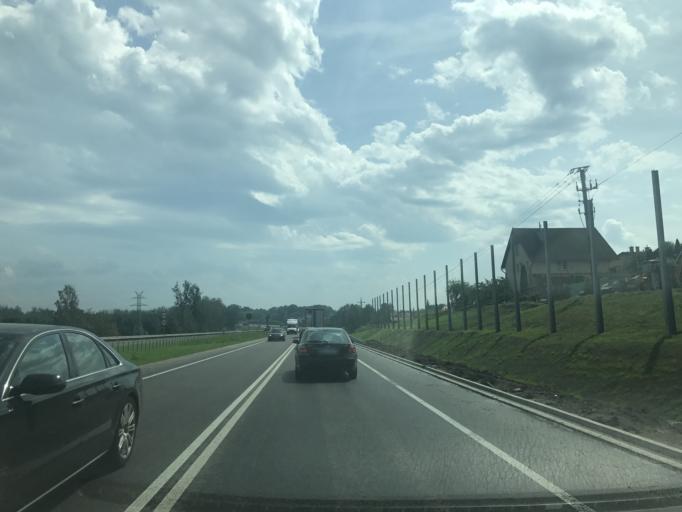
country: PL
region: Warmian-Masurian Voivodeship
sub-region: Powiat ostrodzki
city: Ostroda
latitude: 53.6971
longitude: 19.9826
